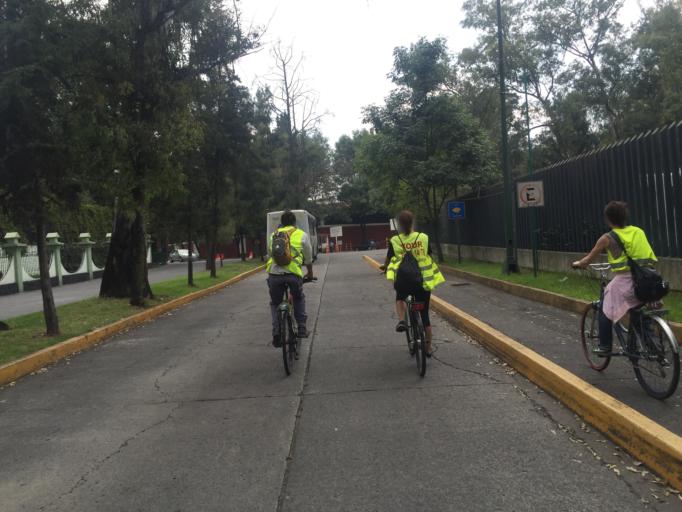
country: MX
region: Mexico City
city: Polanco
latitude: 19.4224
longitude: -99.1939
